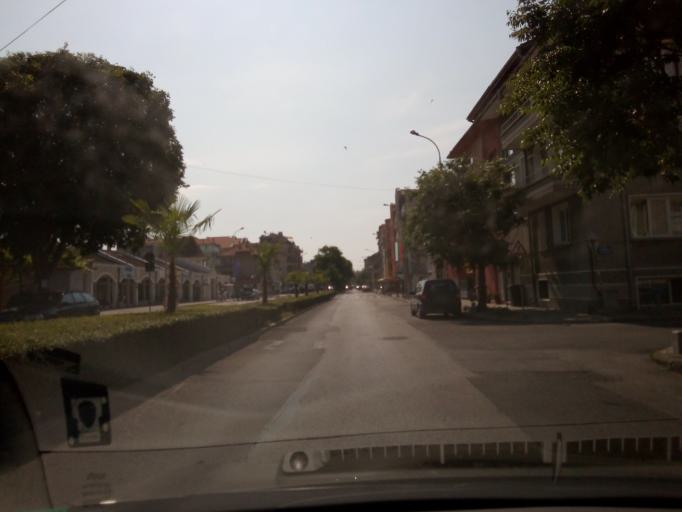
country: BG
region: Burgas
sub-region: Obshtina Pomorie
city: Pomorie
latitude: 42.5610
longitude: 27.6343
